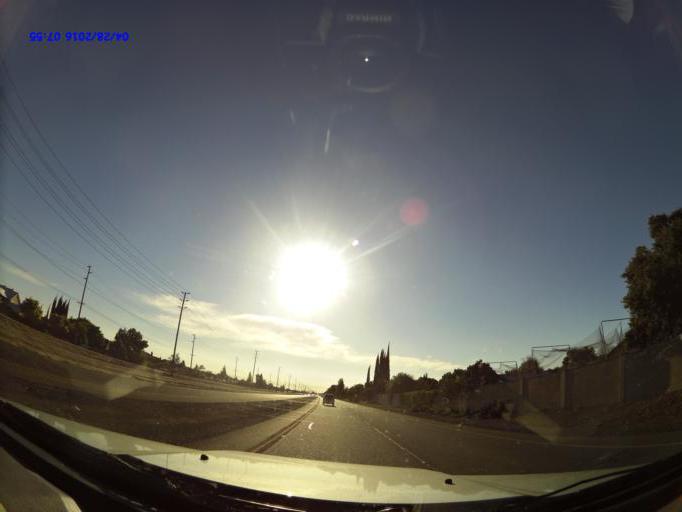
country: US
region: California
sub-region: Stanislaus County
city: Empire
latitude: 37.6668
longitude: -120.9454
